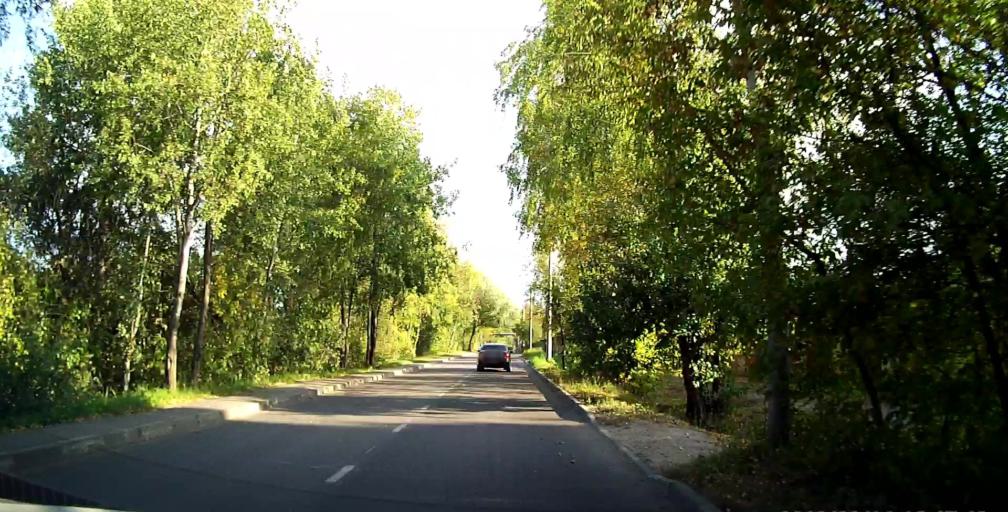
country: RU
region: Moskovskaya
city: Klimovsk
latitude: 55.3632
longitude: 37.5513
